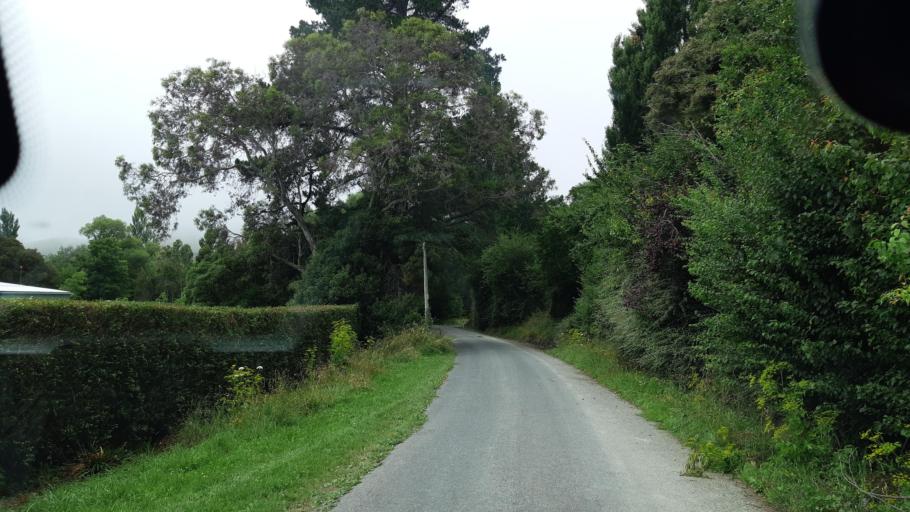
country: NZ
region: Marlborough
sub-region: Marlborough District
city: Blenheim
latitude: -41.9964
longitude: 173.9959
